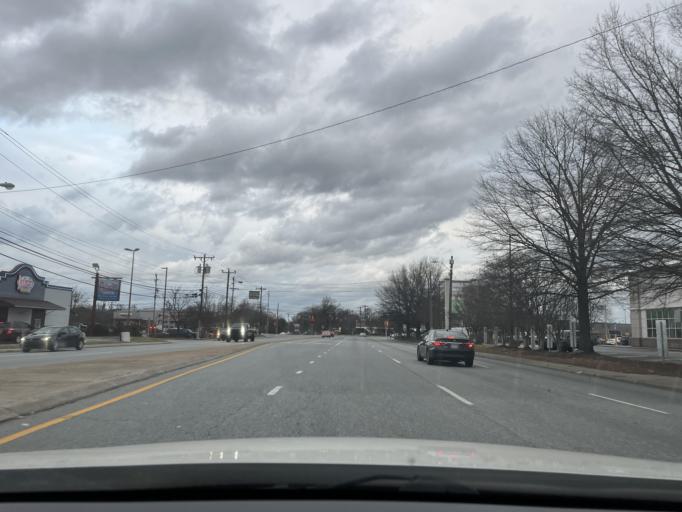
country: US
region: North Carolina
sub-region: Guilford County
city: Greensboro
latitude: 36.0384
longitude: -79.8497
